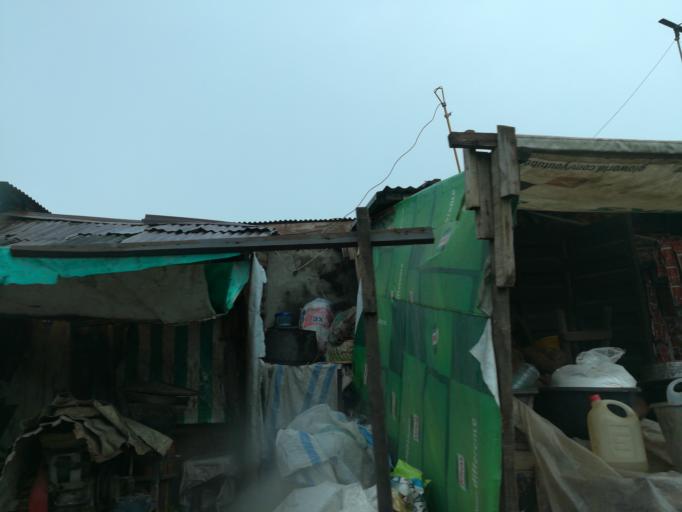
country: NG
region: Lagos
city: Oshodi
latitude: 6.5603
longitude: 3.3380
